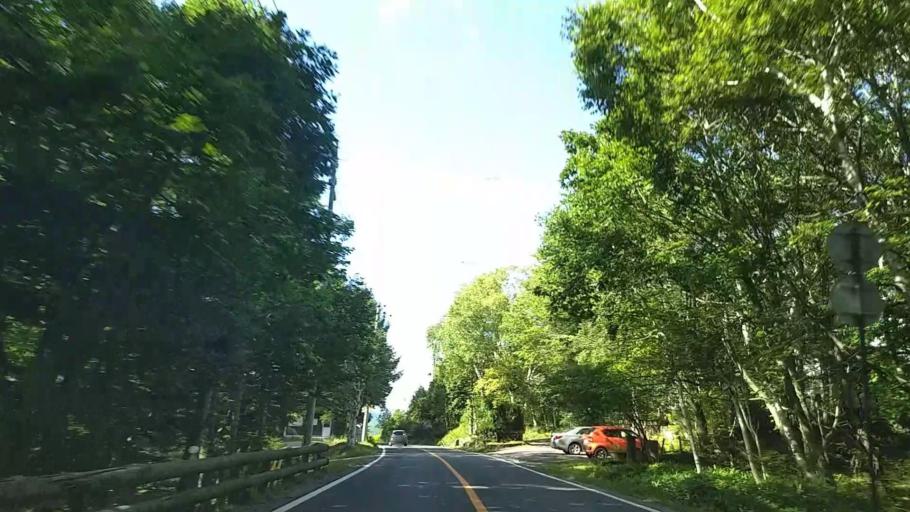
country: JP
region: Nagano
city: Chino
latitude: 36.1052
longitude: 138.2462
